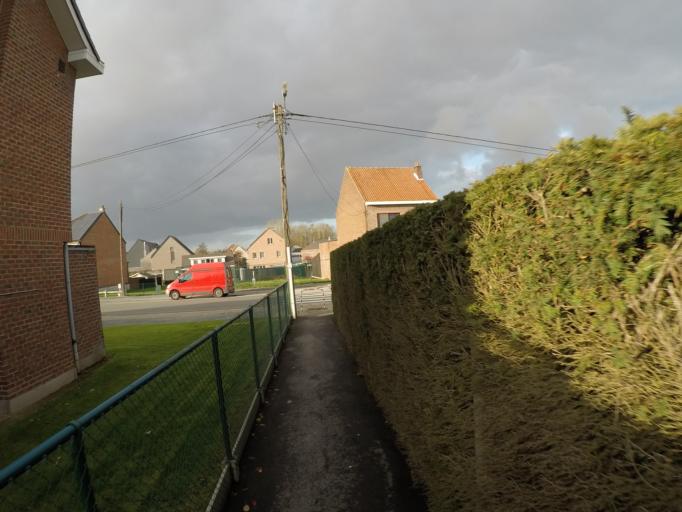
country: BE
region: Flanders
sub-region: Provincie Vlaams-Brabant
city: Opwijk
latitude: 50.9643
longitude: 4.1904
